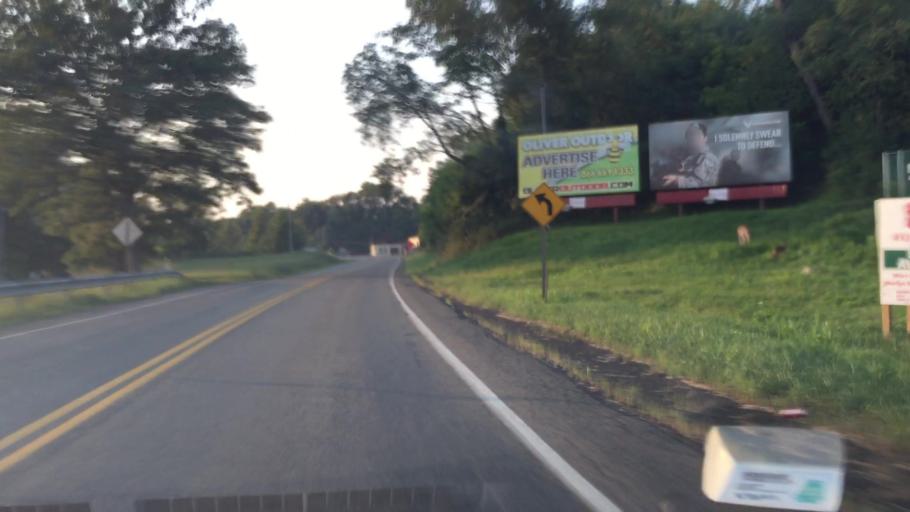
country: US
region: Pennsylvania
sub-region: Butler County
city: Evans City
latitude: 40.7473
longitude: -80.0356
